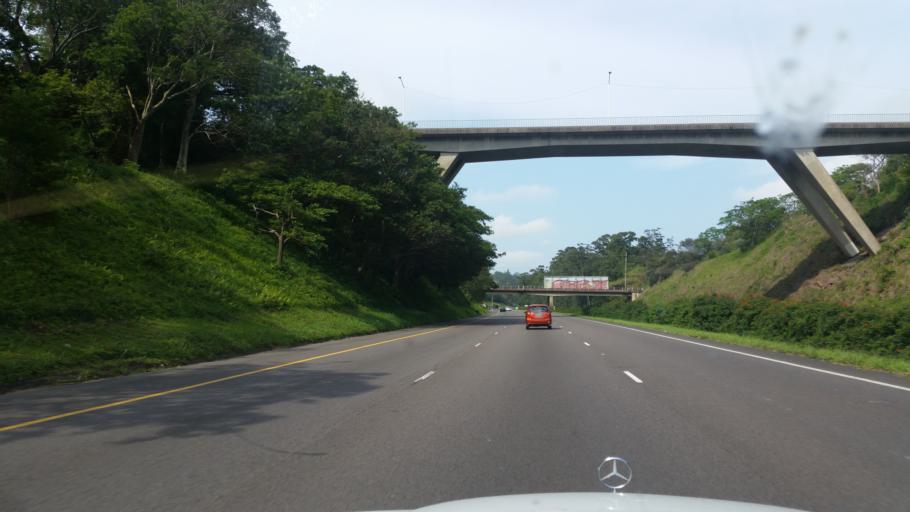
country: ZA
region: KwaZulu-Natal
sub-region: eThekwini Metropolitan Municipality
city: Berea
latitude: -29.8371
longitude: 30.8748
